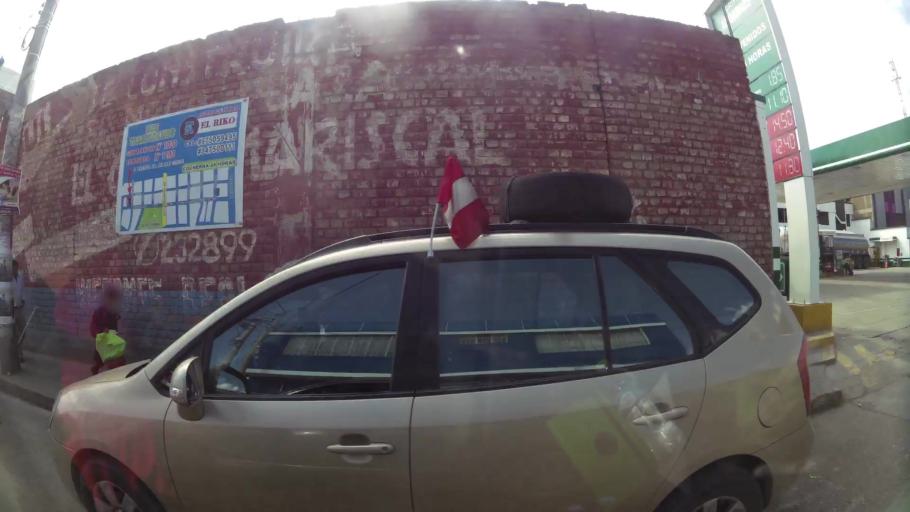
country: PE
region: Junin
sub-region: Provincia de Huancayo
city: Huancayo
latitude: -12.0753
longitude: -75.2072
